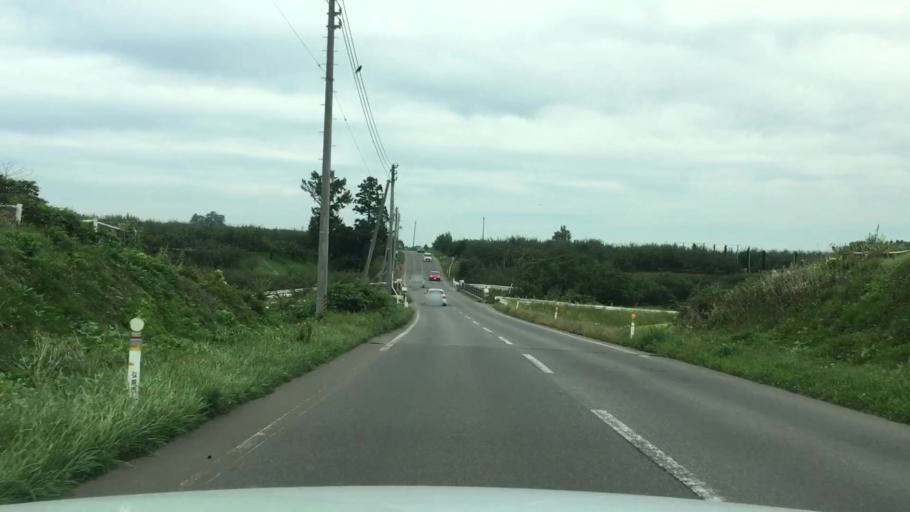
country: JP
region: Aomori
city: Hirosaki
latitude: 40.6550
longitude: 140.4208
